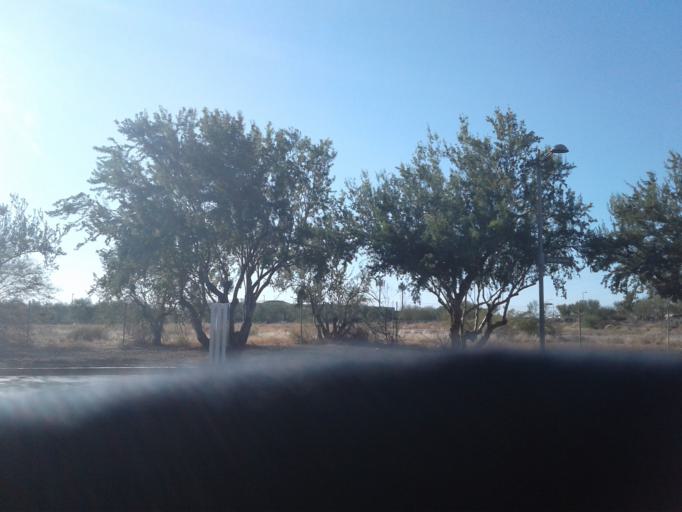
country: US
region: Arizona
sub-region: Maricopa County
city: Paradise Valley
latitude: 33.6766
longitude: -111.9669
